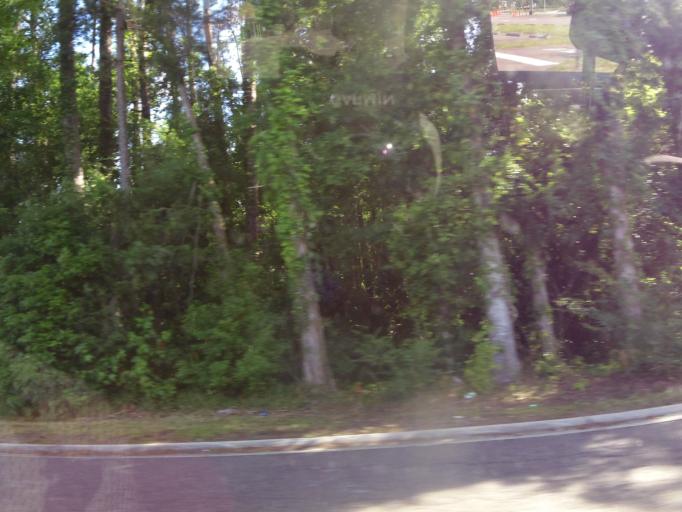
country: US
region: Florida
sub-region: Nassau County
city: Callahan
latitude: 30.5602
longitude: -81.8320
